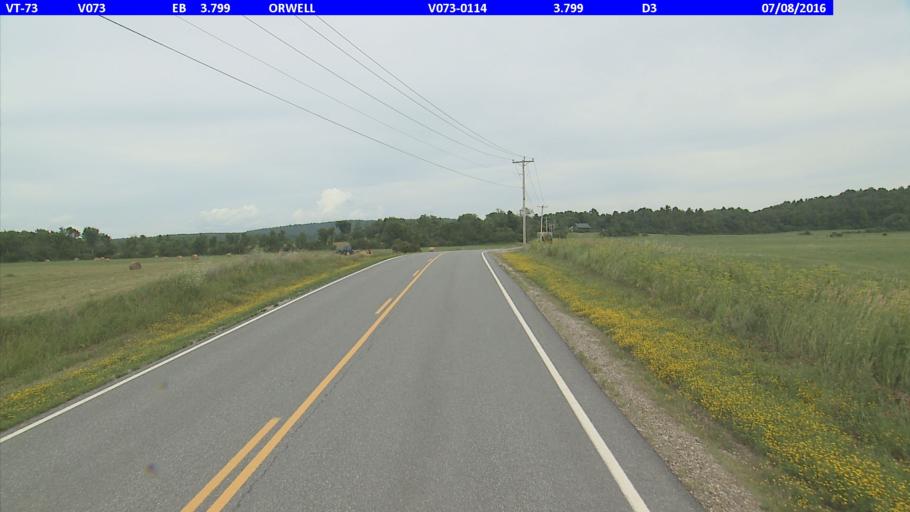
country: US
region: Vermont
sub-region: Rutland County
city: Brandon
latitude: 43.7976
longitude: -73.2340
